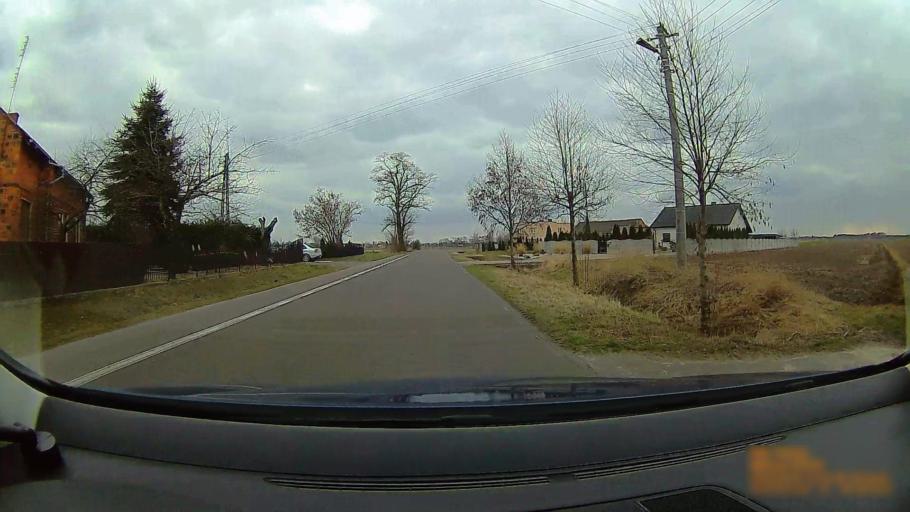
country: PL
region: Greater Poland Voivodeship
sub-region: Powiat koninski
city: Rzgow Pierwszy
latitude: 52.1177
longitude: 18.0710
